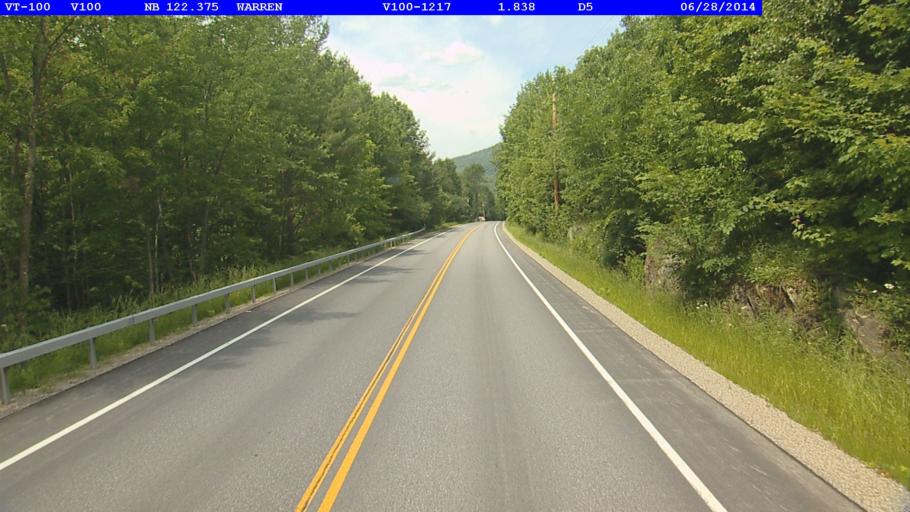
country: US
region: Vermont
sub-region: Washington County
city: Northfield
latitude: 44.0856
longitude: -72.8611
